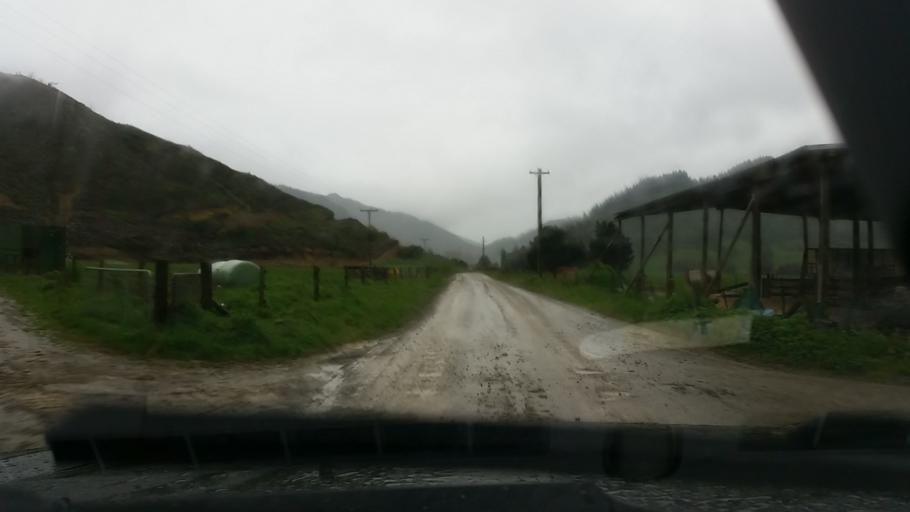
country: NZ
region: Marlborough
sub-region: Marlborough District
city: Picton
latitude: -41.3385
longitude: 173.9278
